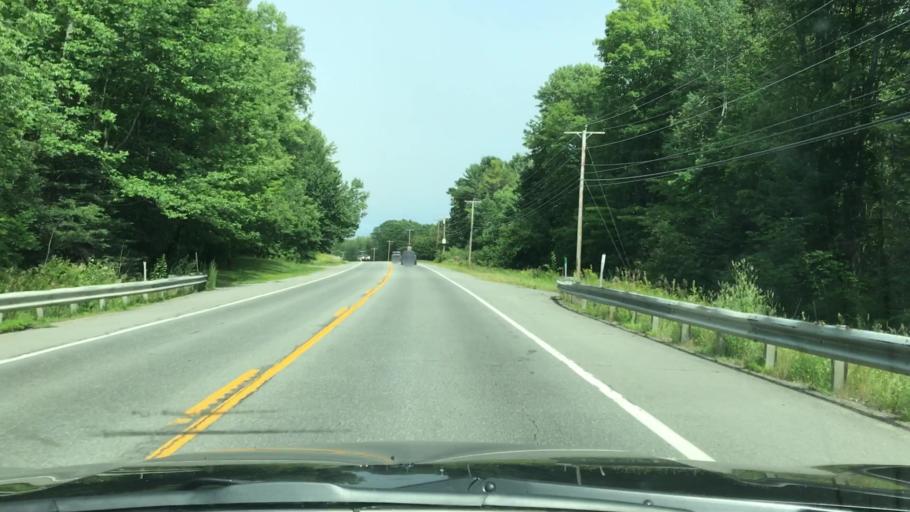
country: US
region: Maine
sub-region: Waldo County
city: Belfast
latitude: 44.4347
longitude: -68.9478
